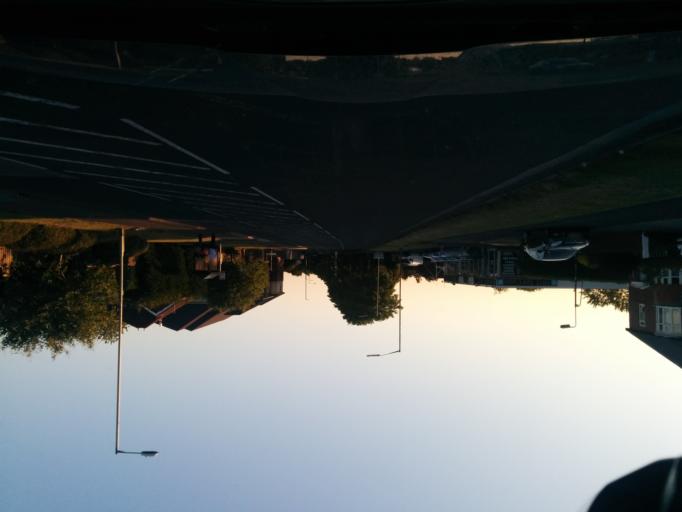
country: GB
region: England
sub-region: Northumberland
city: Bedlington
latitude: 55.1341
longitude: -1.5997
